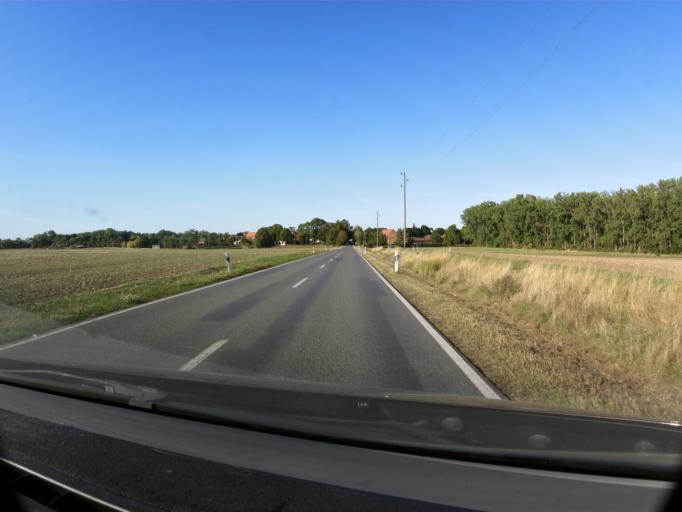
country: DE
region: Saxony-Anhalt
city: Groeningen
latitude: 51.9142
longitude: 11.1933
